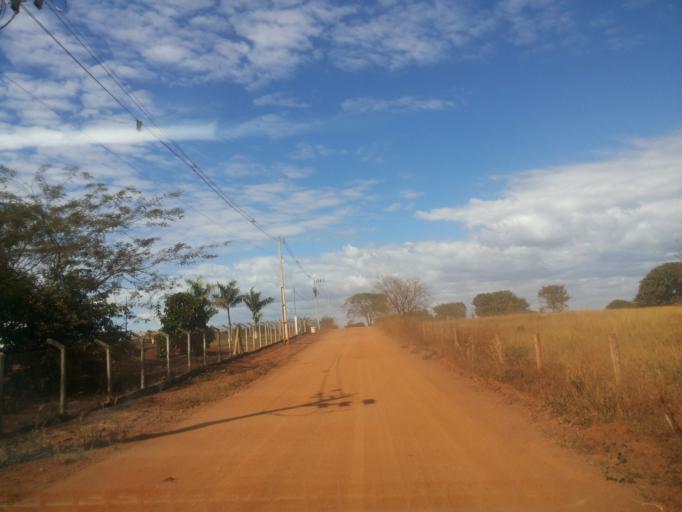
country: BR
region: Minas Gerais
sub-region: Centralina
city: Centralina
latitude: -18.5780
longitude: -49.2129
